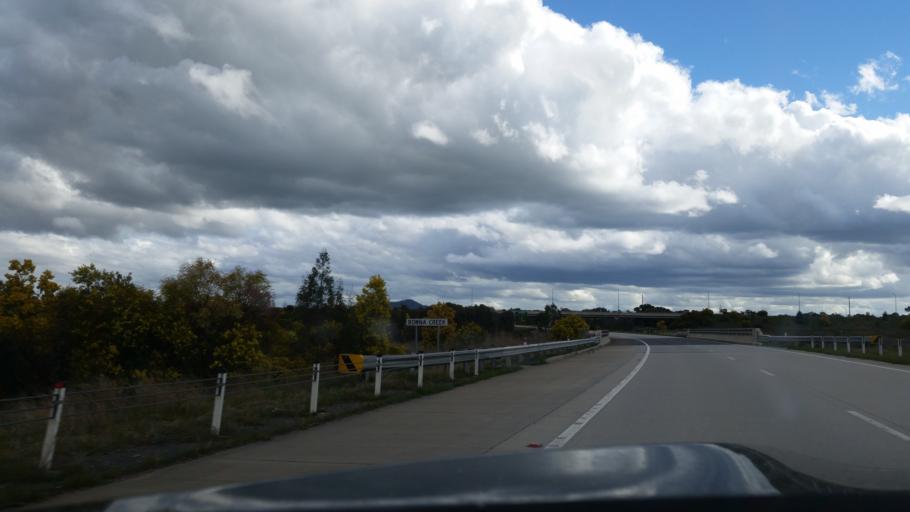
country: AU
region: New South Wales
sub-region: Greater Hume Shire
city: Jindera
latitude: -35.9252
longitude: 147.0111
